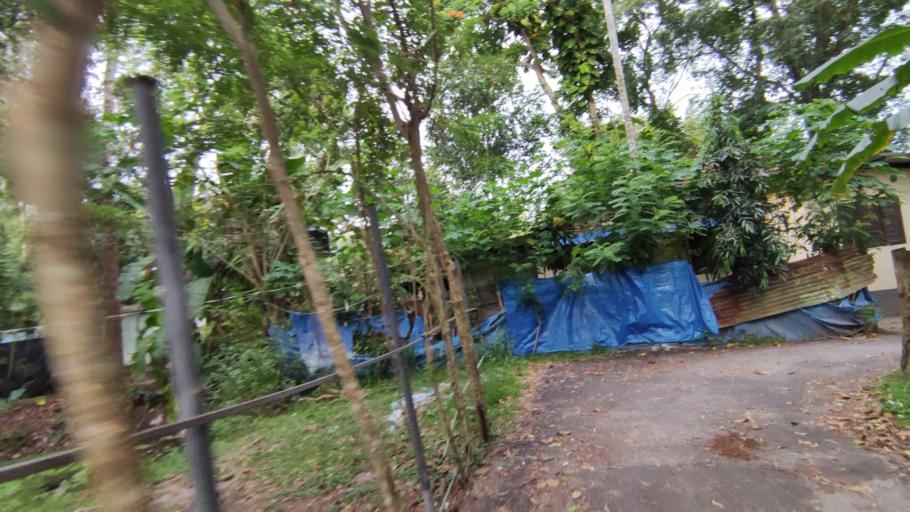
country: IN
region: Kerala
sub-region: Alappuzha
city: Shertallai
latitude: 9.6164
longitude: 76.3468
